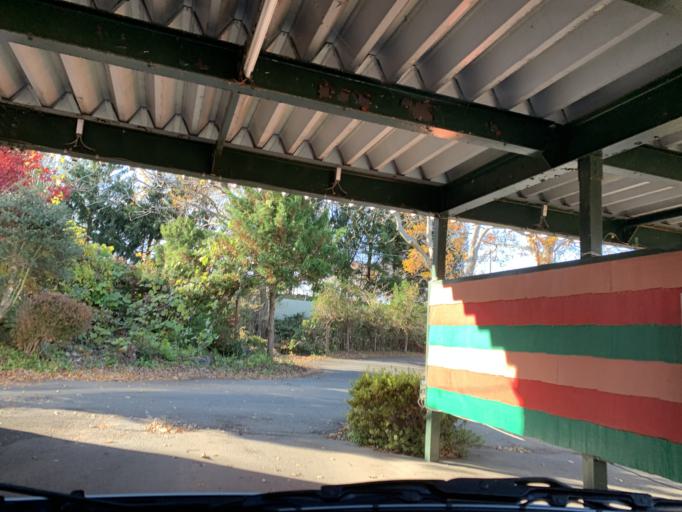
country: JP
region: Iwate
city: Kitakami
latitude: 39.2503
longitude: 141.0939
